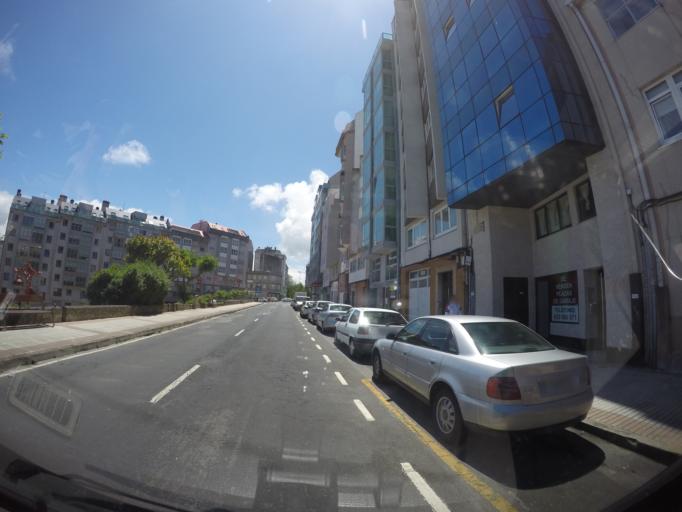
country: ES
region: Galicia
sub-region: Provincia da Coruna
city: A Coruna
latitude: 43.3801
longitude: -8.3993
